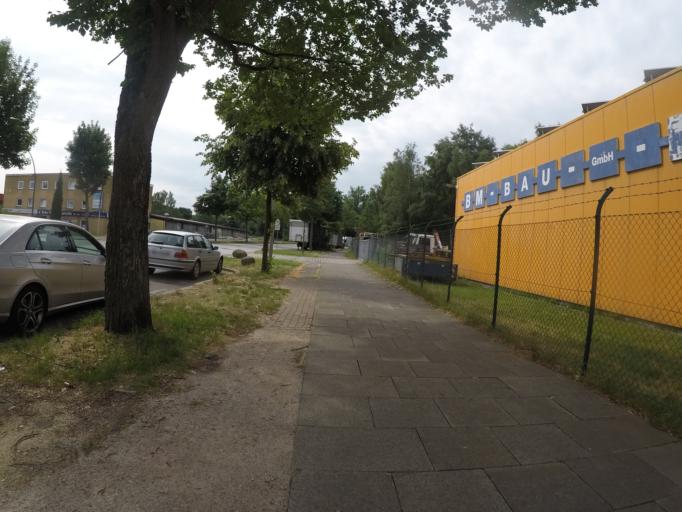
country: DE
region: Hamburg
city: Kleiner Grasbrook
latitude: 53.5168
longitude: 10.0007
